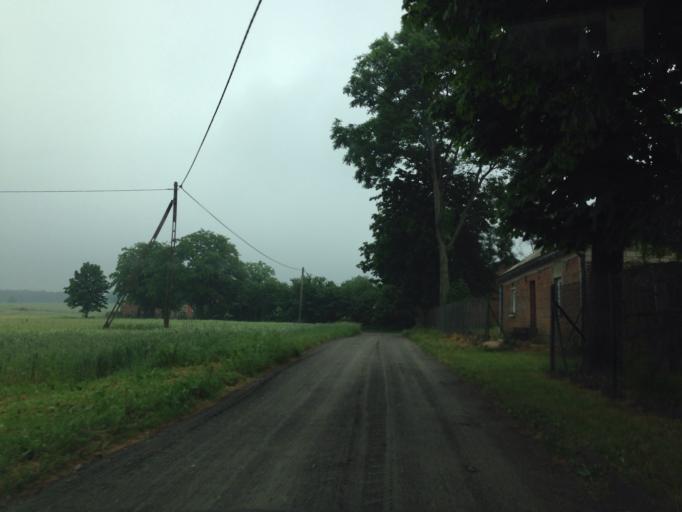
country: PL
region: Kujawsko-Pomorskie
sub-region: Powiat brodnicki
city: Brodnica
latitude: 53.3081
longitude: 19.3576
